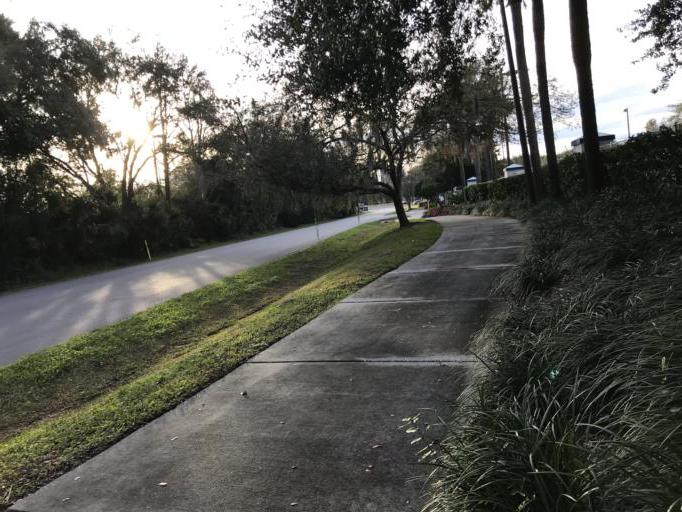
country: US
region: Florida
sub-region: Osceola County
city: Celebration
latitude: 28.3615
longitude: -81.4980
